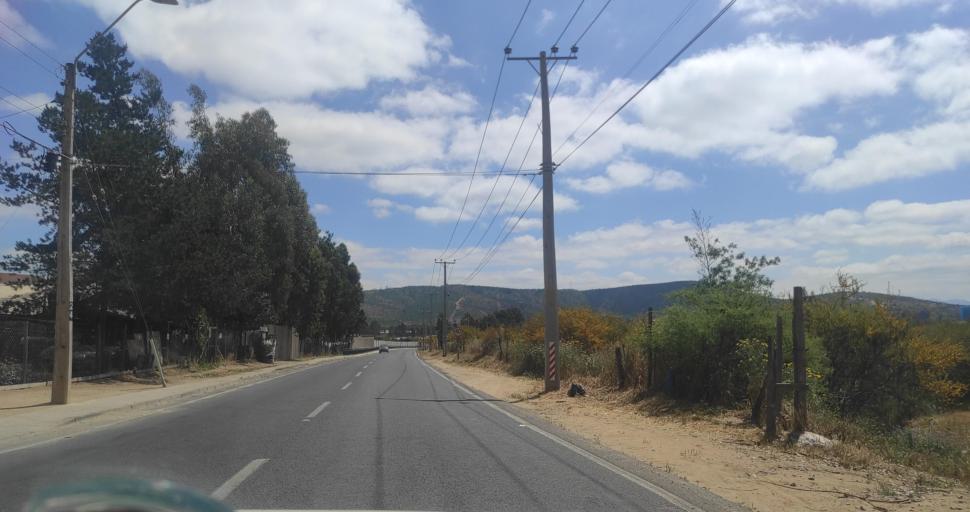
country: CL
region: Valparaiso
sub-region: Provincia de Marga Marga
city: Limache
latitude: -33.0225
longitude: -71.2587
